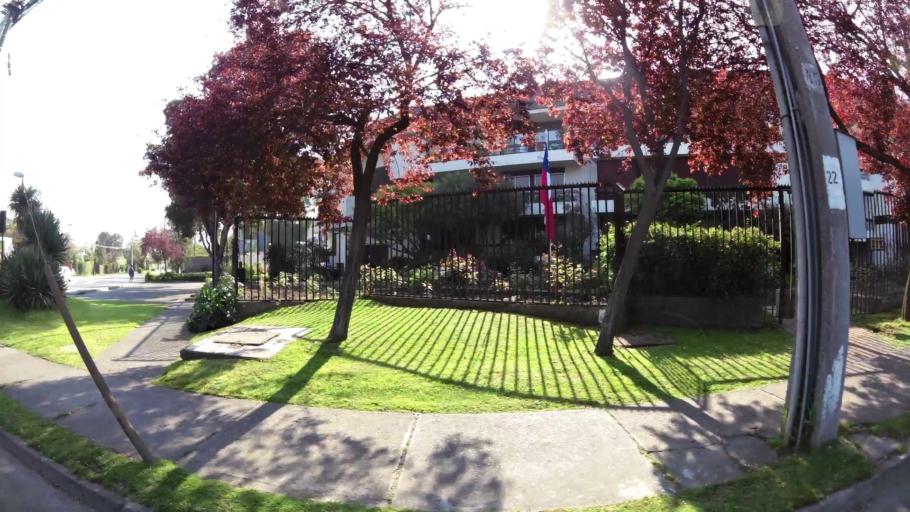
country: CL
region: Santiago Metropolitan
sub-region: Provincia de Santiago
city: Villa Presidente Frei, Nunoa, Santiago, Chile
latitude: -33.3849
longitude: -70.5666
